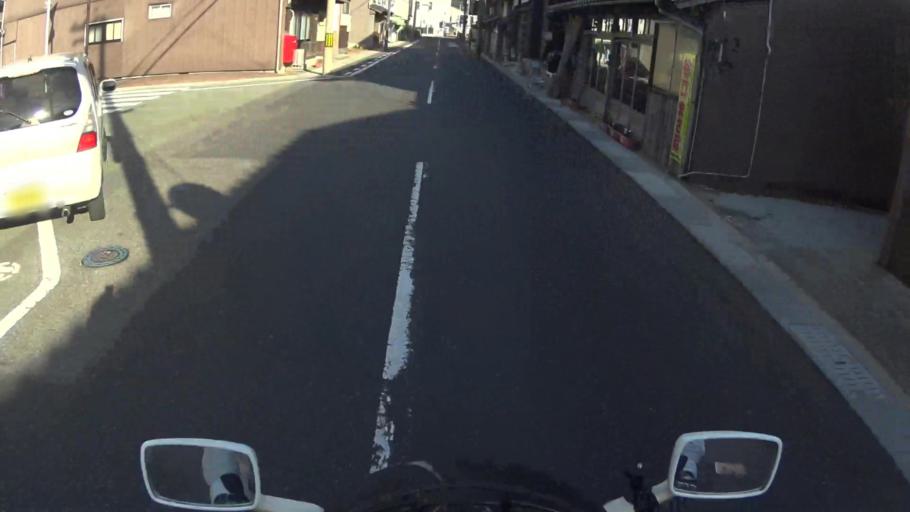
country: JP
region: Hyogo
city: Toyooka
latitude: 35.6069
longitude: 134.8958
